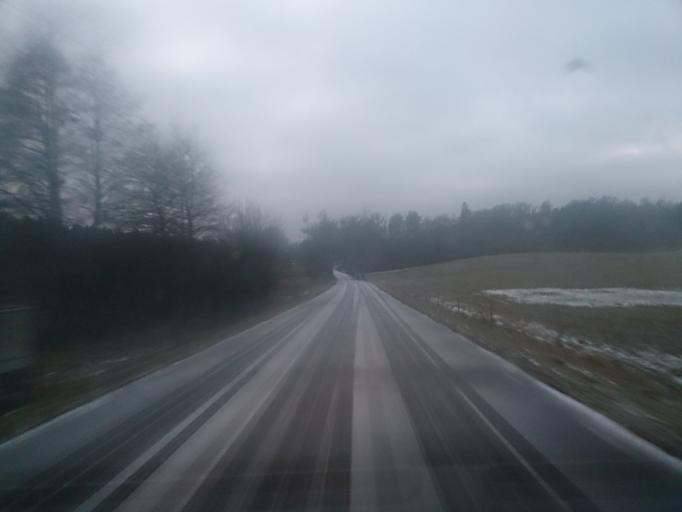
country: SE
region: OEstergoetland
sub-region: Atvidabergs Kommun
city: Atvidaberg
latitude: 58.2777
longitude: 16.1926
